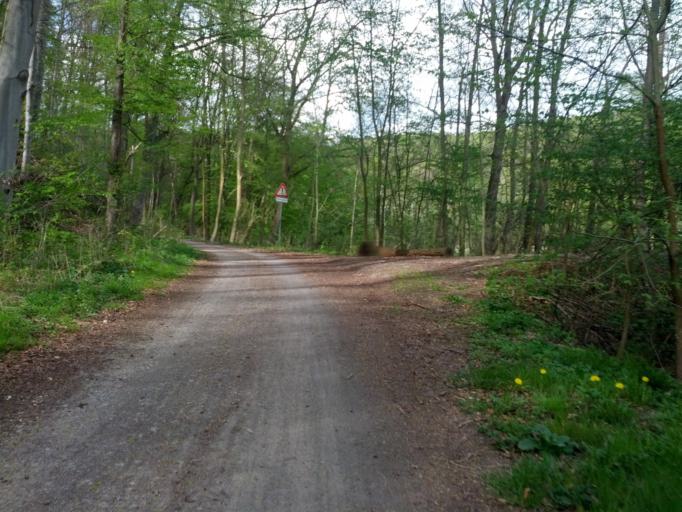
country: DE
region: Thuringia
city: Krauthausen
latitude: 51.0024
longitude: 10.2404
